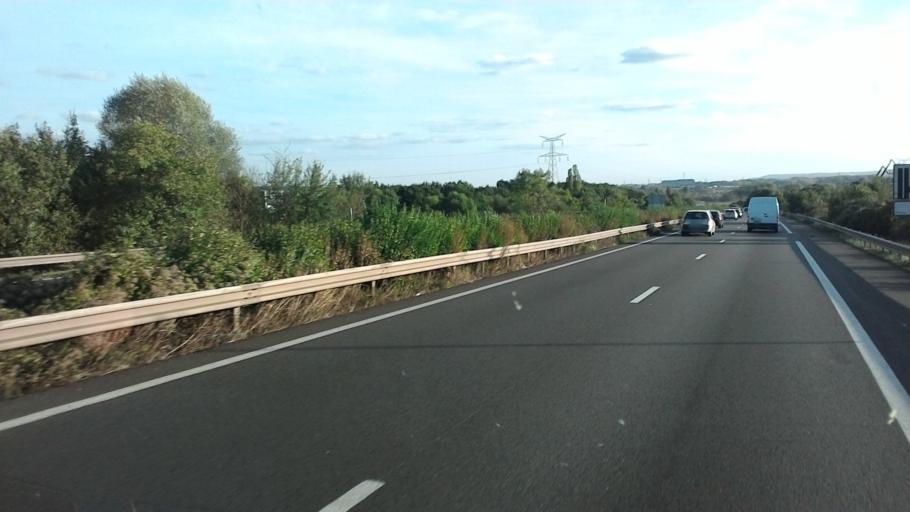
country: FR
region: Lorraine
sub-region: Departement de la Moselle
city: Illange
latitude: 49.3218
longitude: 6.1835
